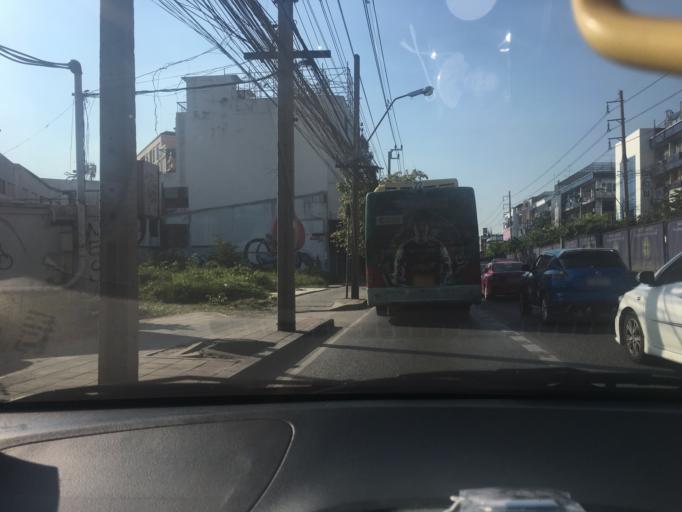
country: TH
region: Bangkok
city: Huai Khwang
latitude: 13.8011
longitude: 100.5824
